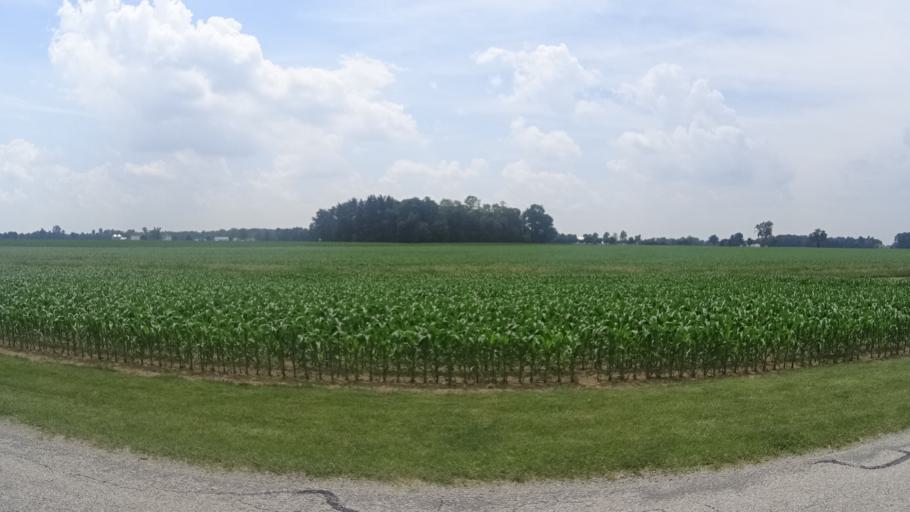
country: US
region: Ohio
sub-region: Erie County
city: Milan
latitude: 41.3153
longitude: -82.6582
